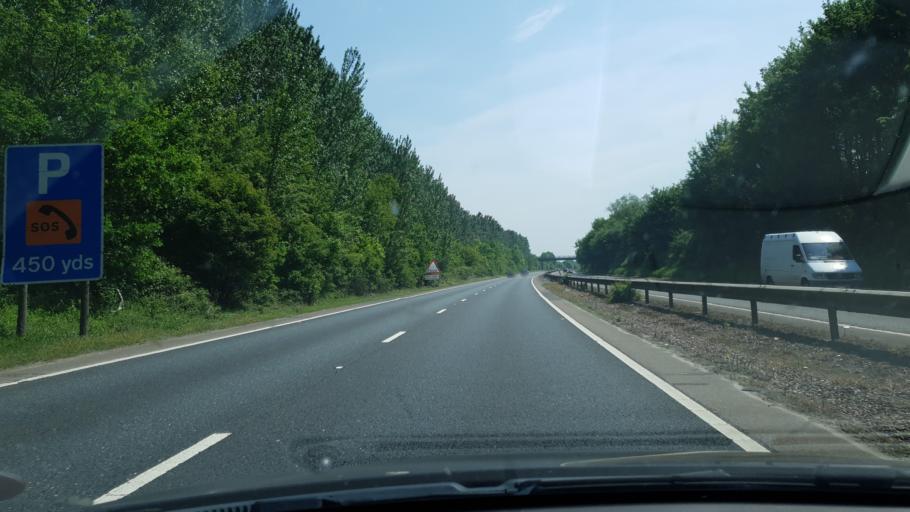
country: GB
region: England
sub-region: Suffolk
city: Thurston
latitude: 52.2369
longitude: 0.8364
